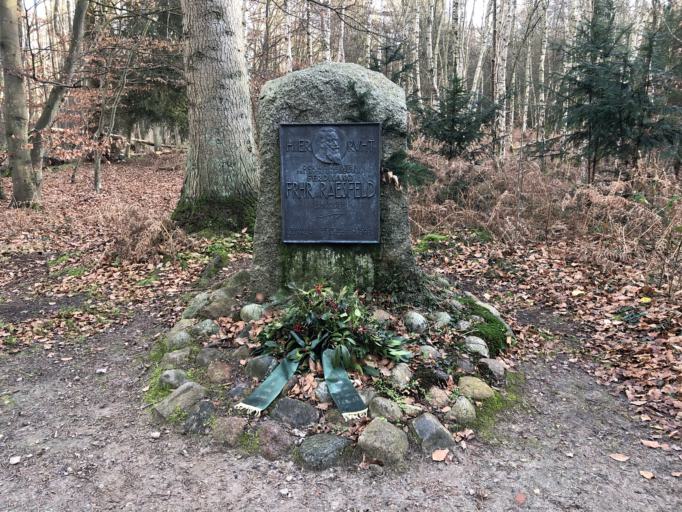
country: DE
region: Mecklenburg-Vorpommern
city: Born
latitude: 54.4259
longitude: 12.5012
